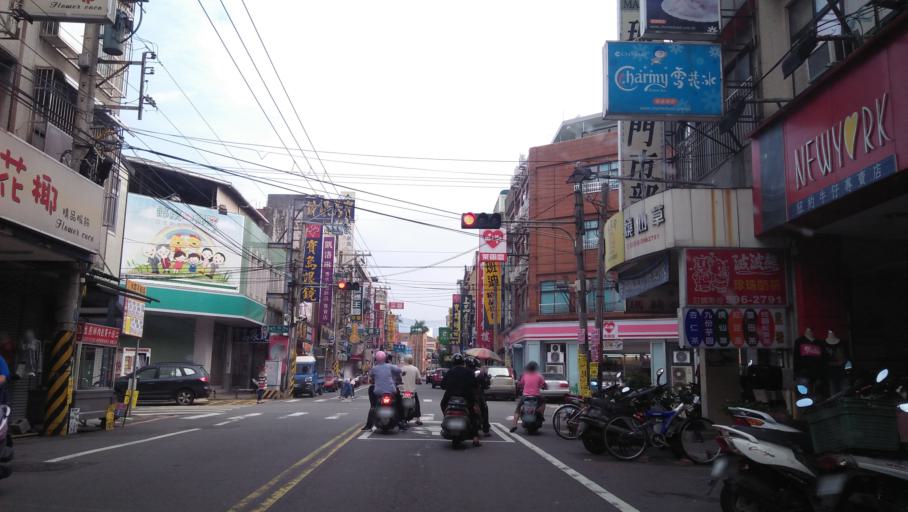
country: TW
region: Taiwan
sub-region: Hsinchu
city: Zhubei
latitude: 24.7385
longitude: 121.0878
